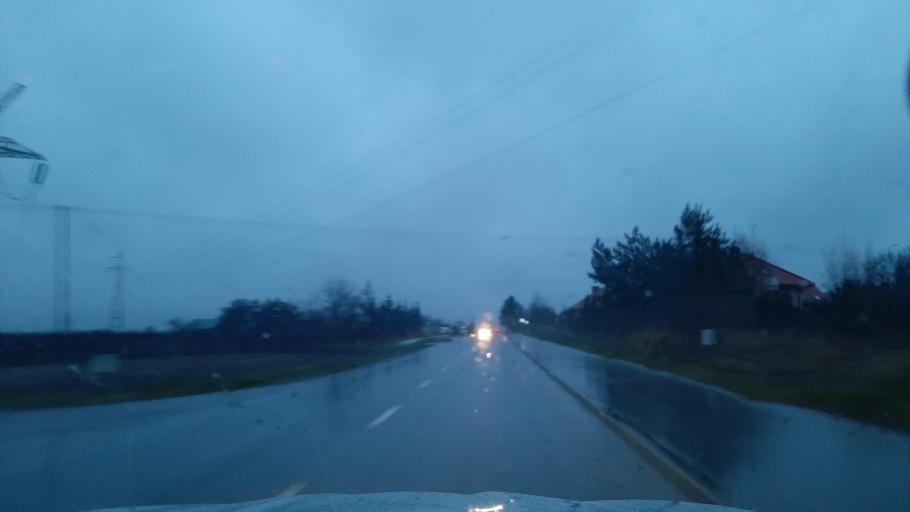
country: PL
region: Lublin Voivodeship
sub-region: Powiat lubelski
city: Jastkow
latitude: 51.3336
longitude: 22.5074
